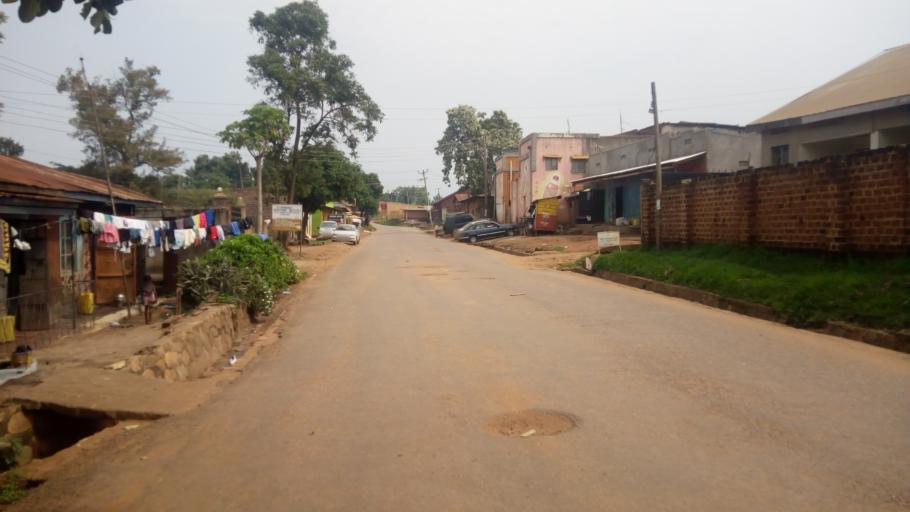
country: UG
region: Central Region
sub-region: Wakiso District
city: Kireka
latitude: 0.3037
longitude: 32.6506
